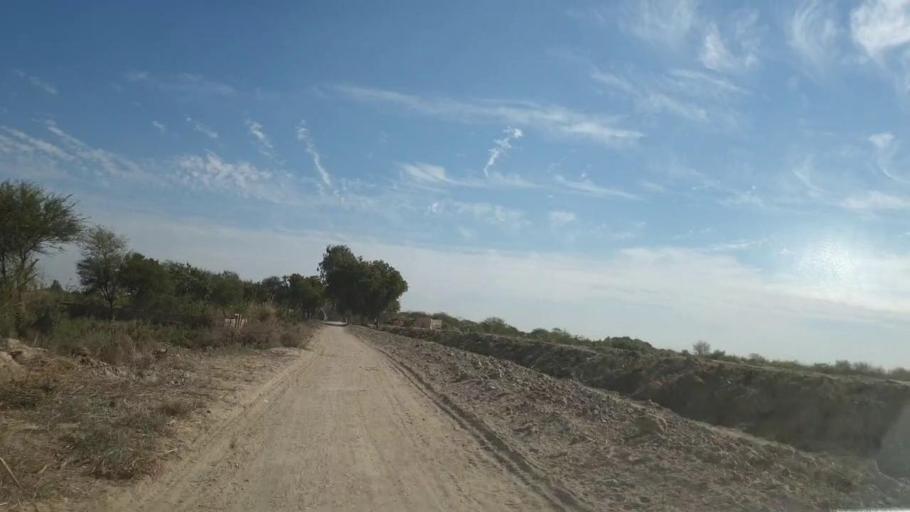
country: PK
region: Sindh
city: Pithoro
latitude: 25.5395
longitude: 69.3022
